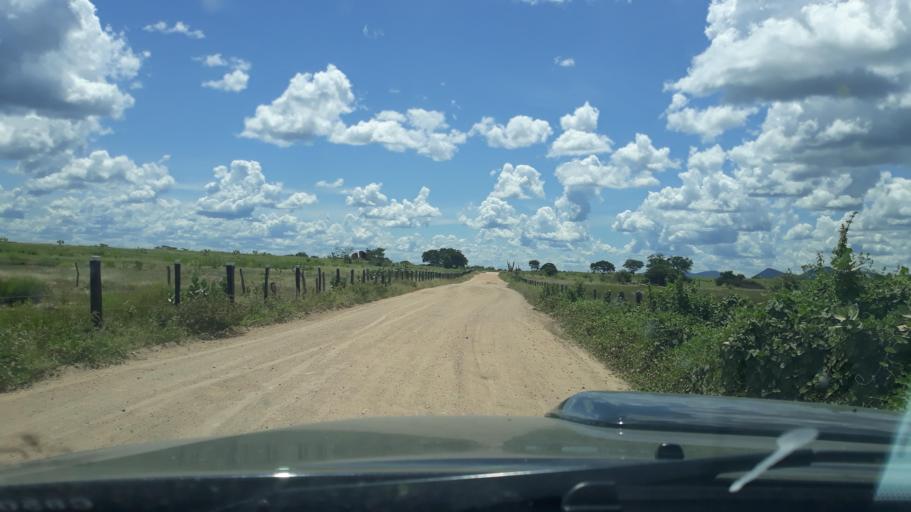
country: BR
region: Bahia
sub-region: Riacho De Santana
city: Riacho de Santana
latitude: -13.9030
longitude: -42.8637
